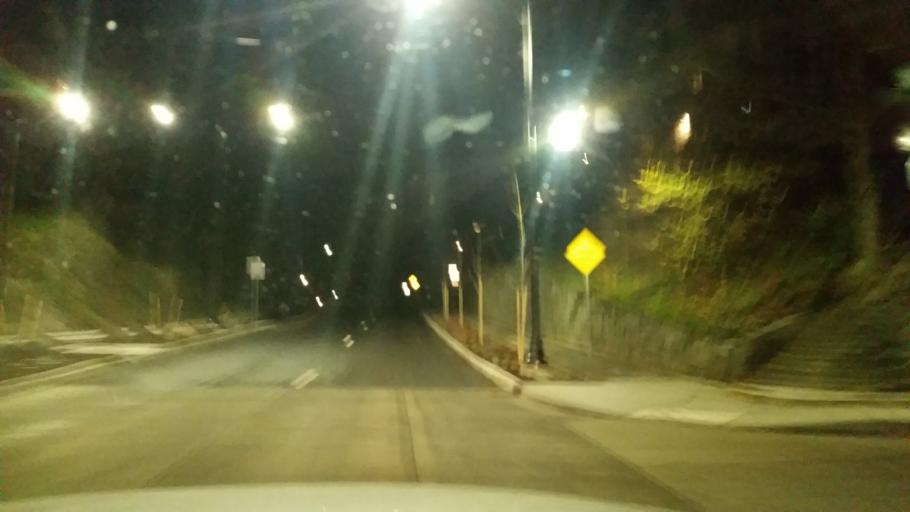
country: US
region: Washington
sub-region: Spokane County
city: Spokane
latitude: 47.6495
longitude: -117.4265
